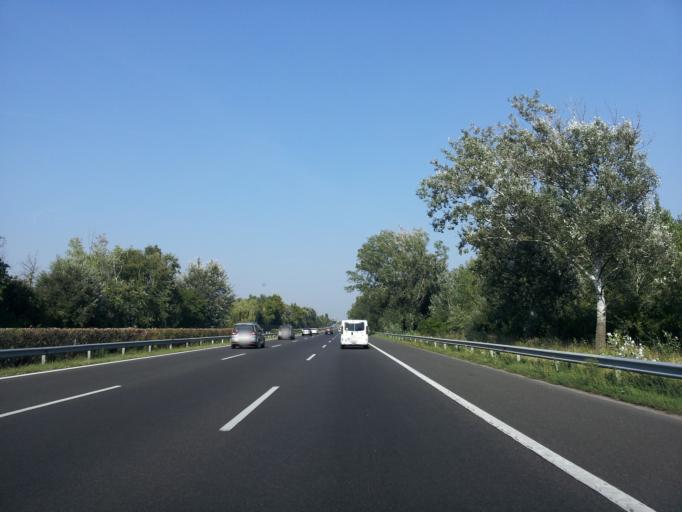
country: HU
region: Fejer
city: Gardony
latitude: 47.2355
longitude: 18.6175
